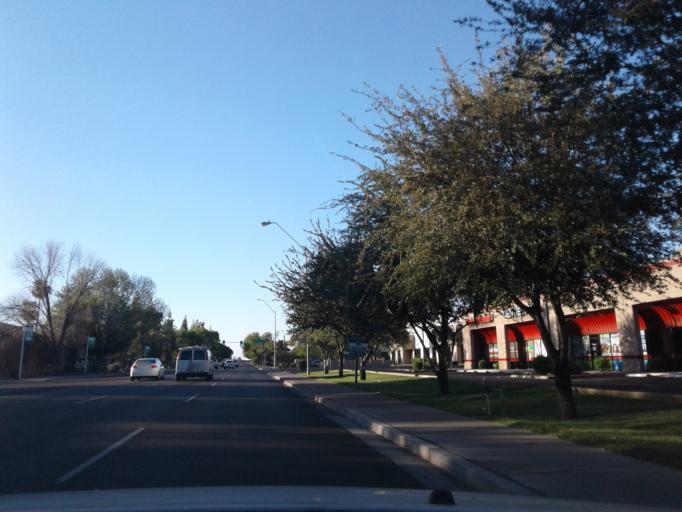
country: US
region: Arizona
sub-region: Maricopa County
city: Phoenix
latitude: 33.4826
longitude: -112.1343
